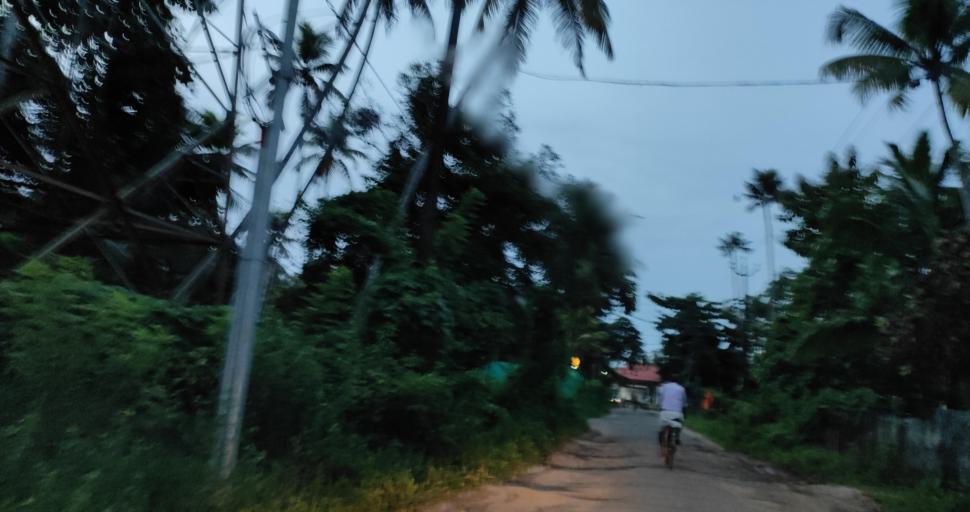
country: IN
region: Kerala
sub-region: Alappuzha
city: Vayalar
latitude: 9.6989
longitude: 76.3134
